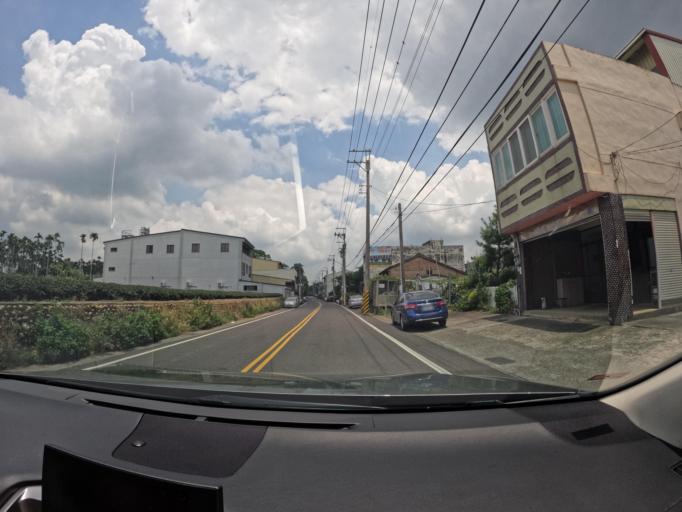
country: TW
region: Taiwan
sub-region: Nantou
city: Nantou
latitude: 23.9041
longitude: 120.6382
